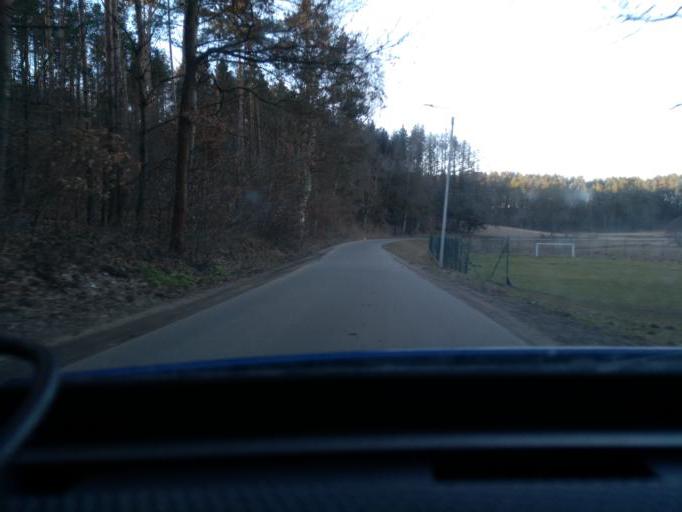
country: PL
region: Pomeranian Voivodeship
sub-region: Powiat kartuski
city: Przodkowo
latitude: 54.3797
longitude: 18.2660
